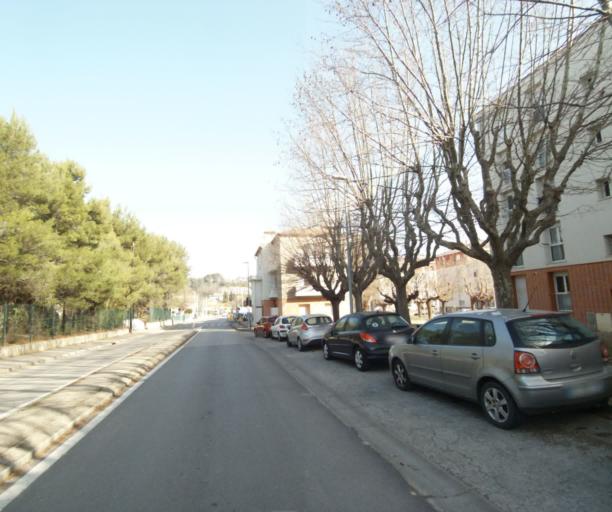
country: FR
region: Provence-Alpes-Cote d'Azur
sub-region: Departement des Bouches-du-Rhone
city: Aix-en-Provence
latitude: 43.5393
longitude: 5.4535
